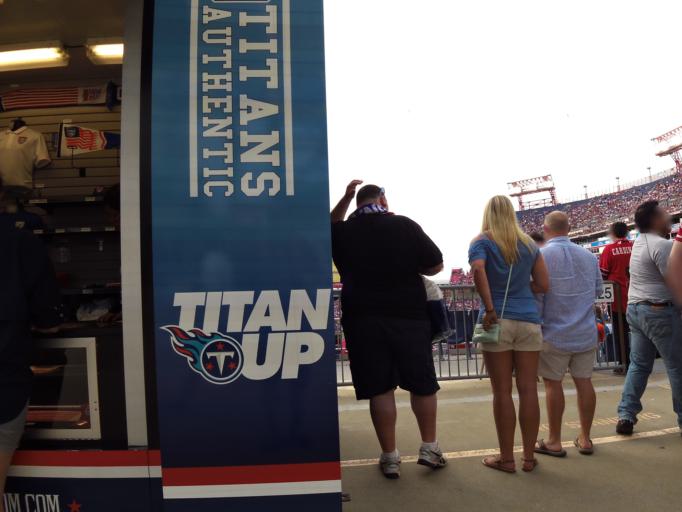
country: US
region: Tennessee
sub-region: Davidson County
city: Nashville
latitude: 36.1656
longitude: -86.7710
